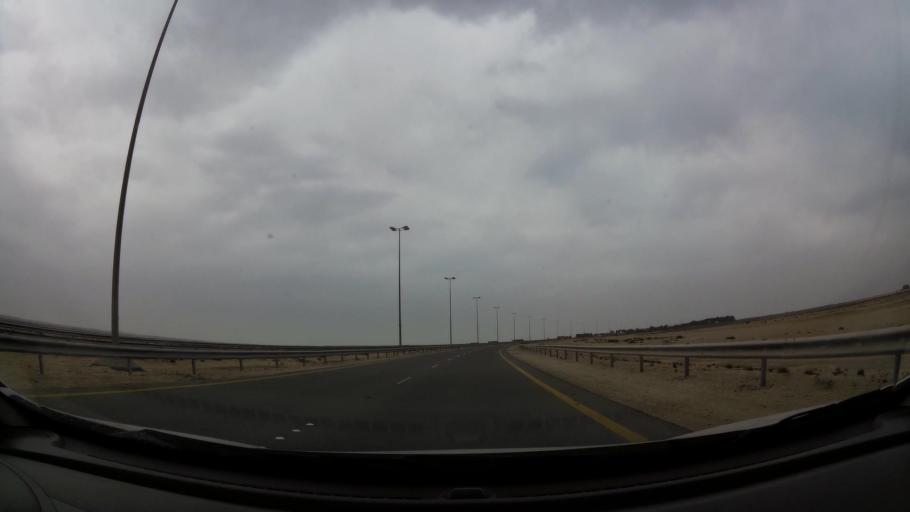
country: BH
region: Central Governorate
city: Dar Kulayb
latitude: 25.9998
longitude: 50.4849
